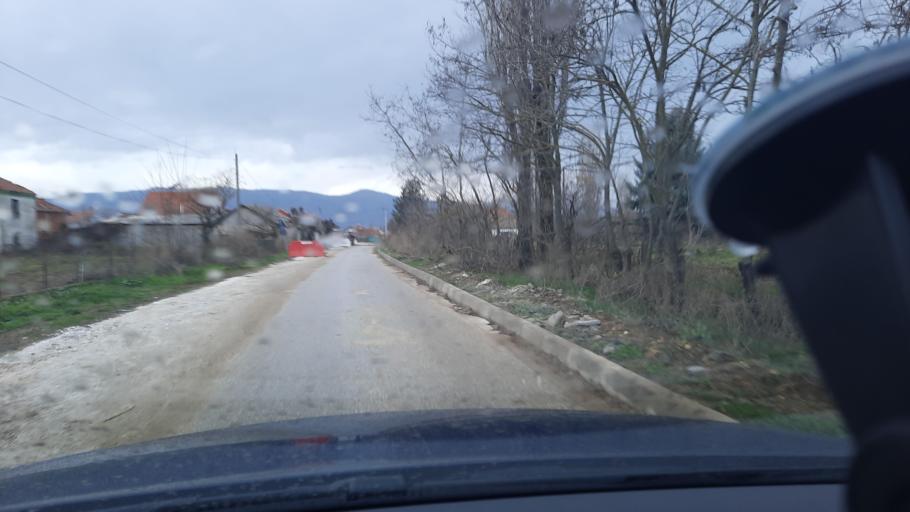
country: MK
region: Mogila
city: Mogila
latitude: 41.1102
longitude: 21.3823
